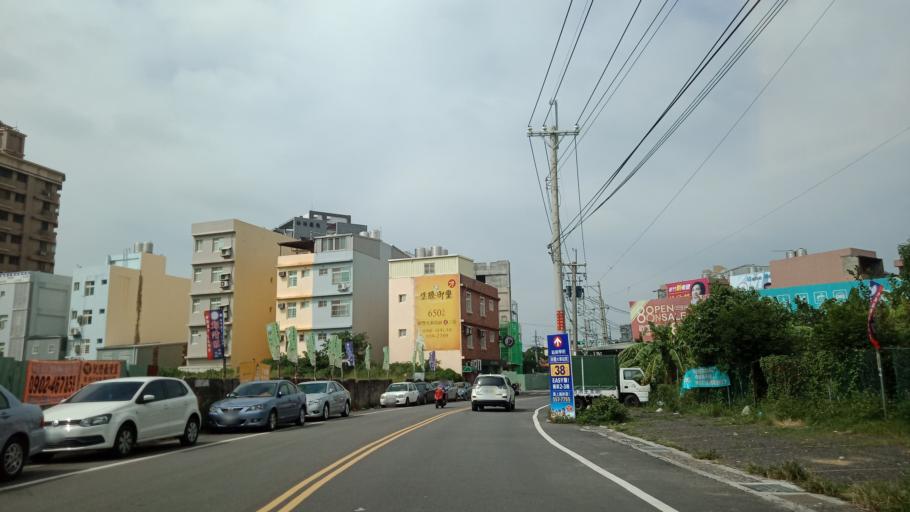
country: TW
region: Taiwan
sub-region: Hsinchu
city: Zhubei
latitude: 24.8712
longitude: 120.9933
